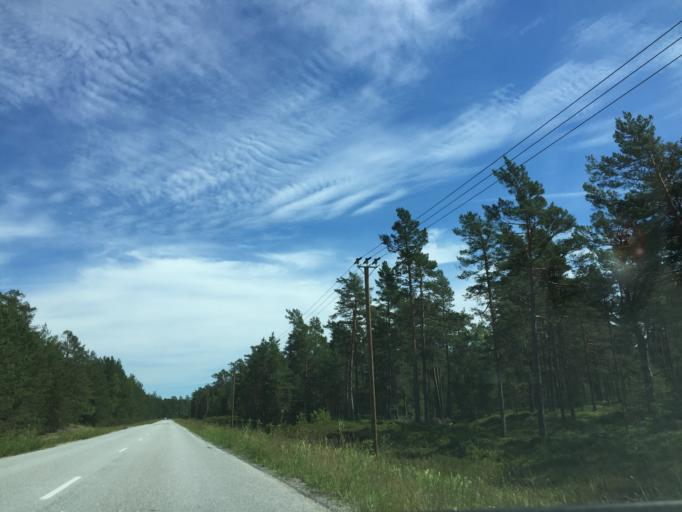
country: LV
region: Rojas
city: Roja
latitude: 57.5724
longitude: 22.6380
